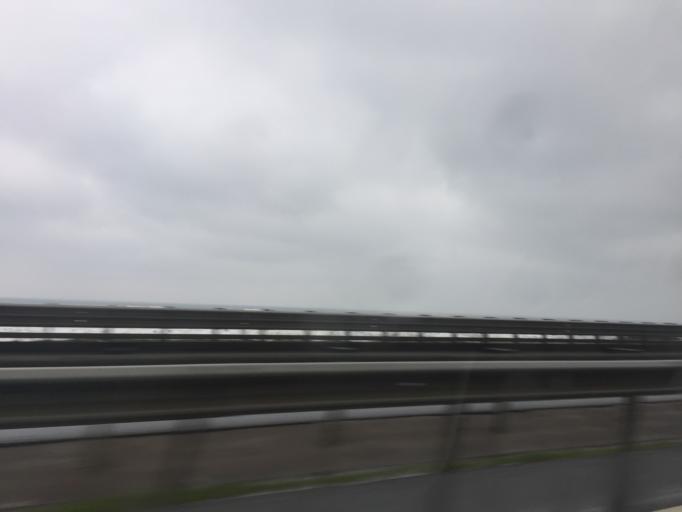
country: TR
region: Zonguldak
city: Alapli
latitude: 41.1101
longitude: 31.2741
